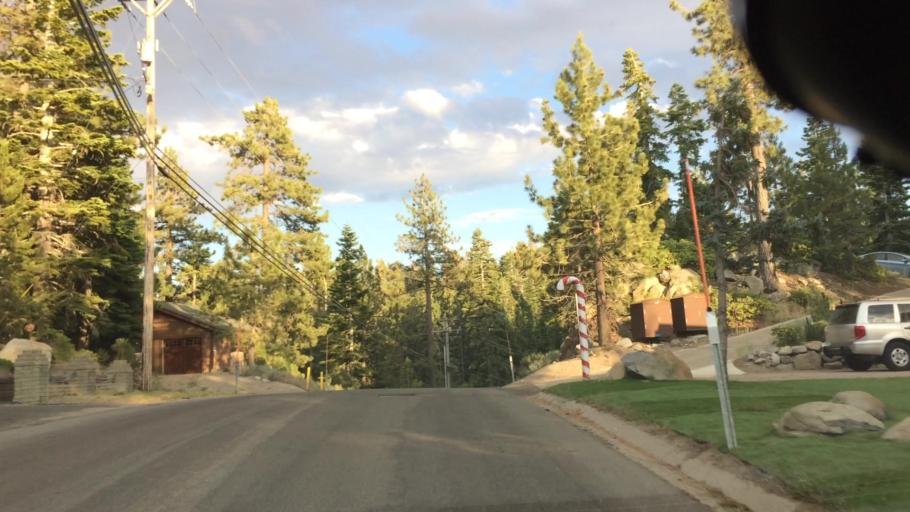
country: US
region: Nevada
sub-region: Douglas County
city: Kingsbury
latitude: 38.9712
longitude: -119.8896
